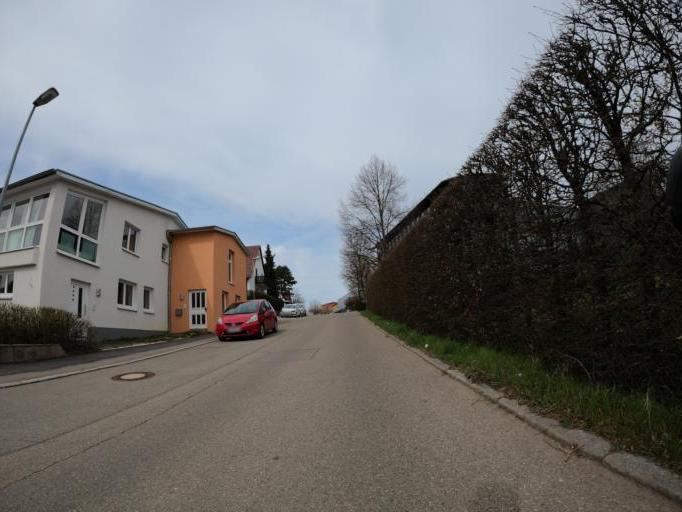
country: DE
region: Baden-Wuerttemberg
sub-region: Regierungsbezirk Stuttgart
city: Wolfschlugen
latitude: 48.6469
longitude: 9.2528
